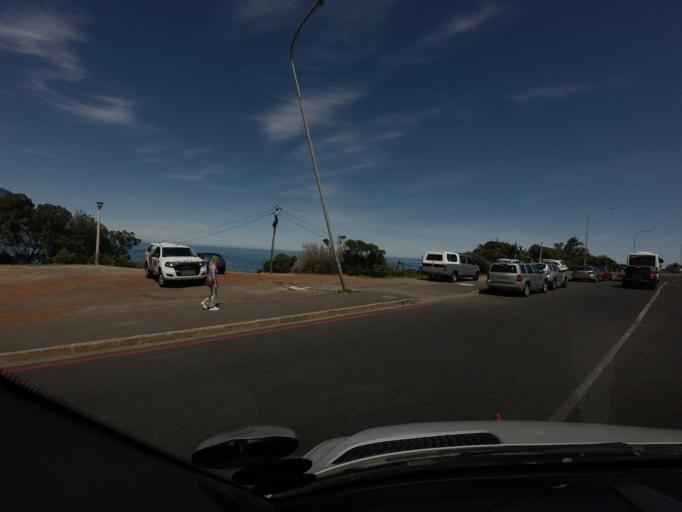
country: ZA
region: Western Cape
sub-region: City of Cape Town
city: Cape Town
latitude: -33.9453
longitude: 18.3778
